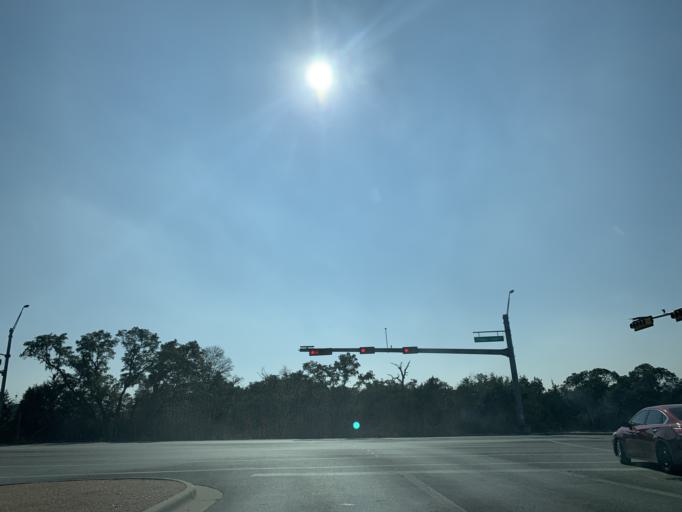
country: US
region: Texas
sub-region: Williamson County
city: Round Rock
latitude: 30.5090
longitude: -97.6365
